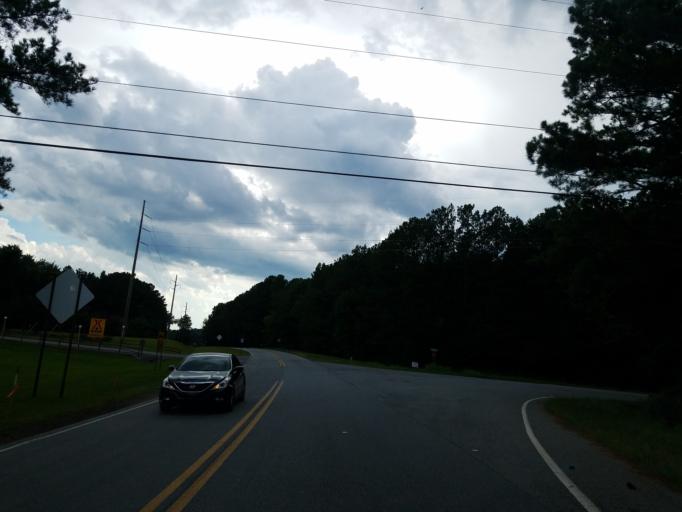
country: US
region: Georgia
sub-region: Bartow County
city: Cartersville
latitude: 34.2728
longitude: -84.8191
